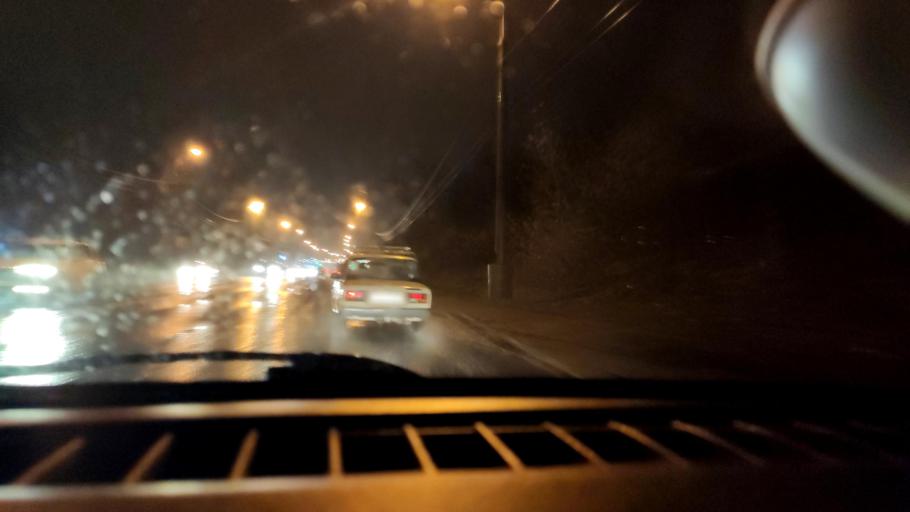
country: RU
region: Samara
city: Samara
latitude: 53.1280
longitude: 50.1712
